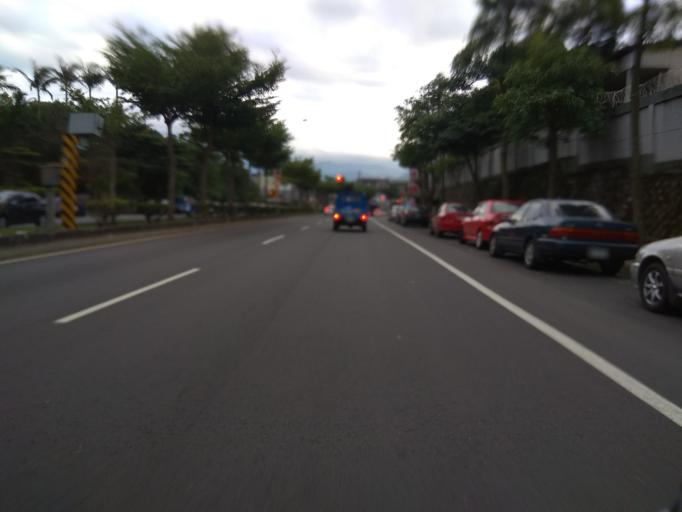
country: TW
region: Taiwan
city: Daxi
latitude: 24.8932
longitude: 121.2118
